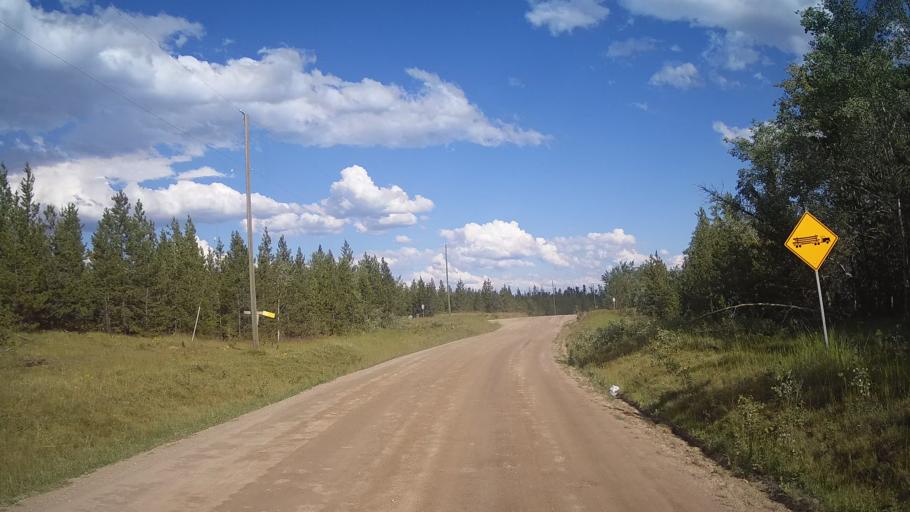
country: CA
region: British Columbia
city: Lillooet
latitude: 51.2830
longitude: -121.7421
